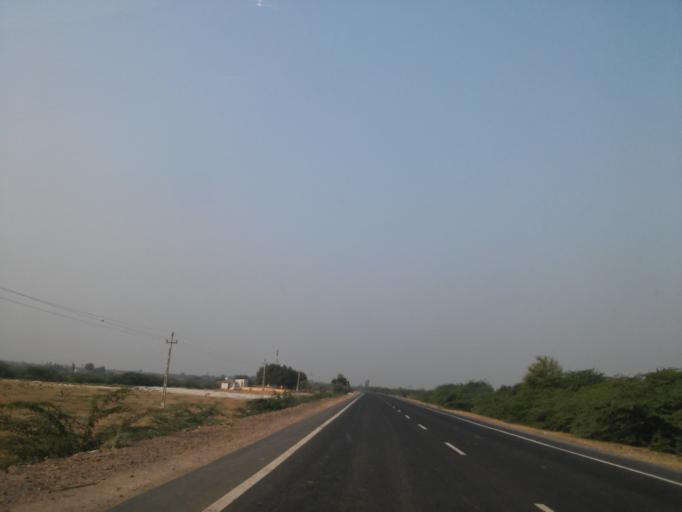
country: IN
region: Gujarat
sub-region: Kachchh
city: Anjar
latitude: 23.2873
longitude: 70.0094
